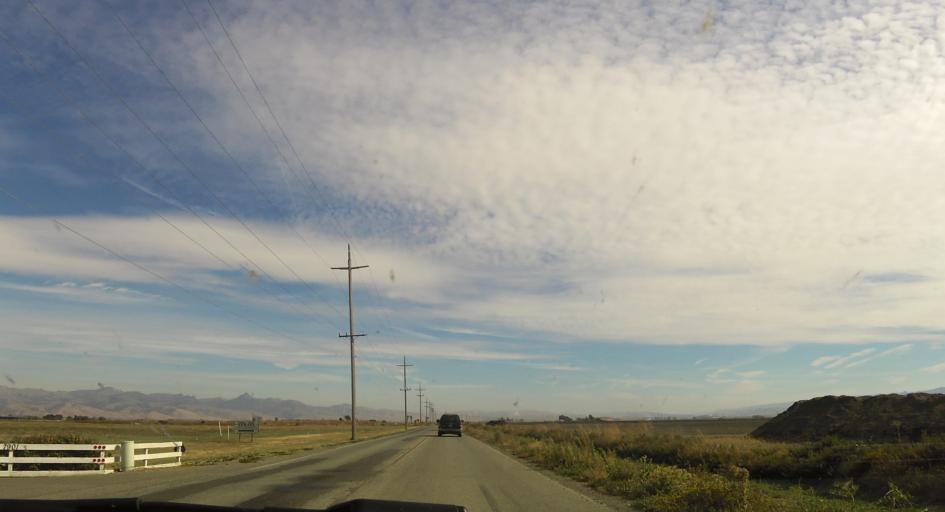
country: US
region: California
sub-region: Santa Clara County
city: Gilroy
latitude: 36.9517
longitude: -121.4741
